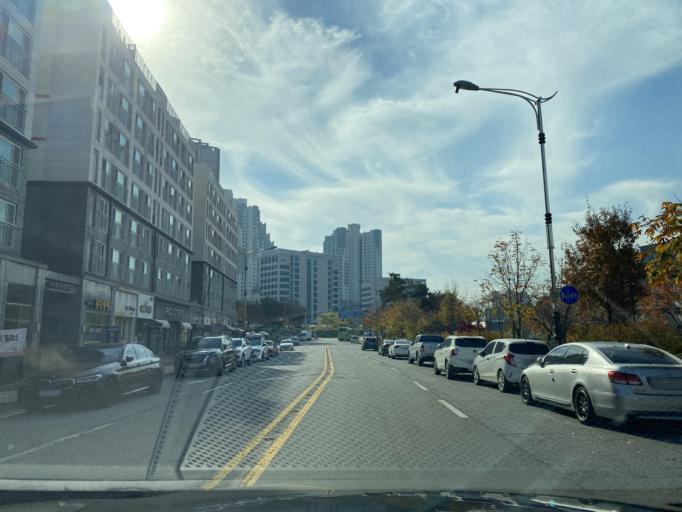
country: KR
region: Chungcheongnam-do
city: Cheonan
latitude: 36.8014
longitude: 127.1086
